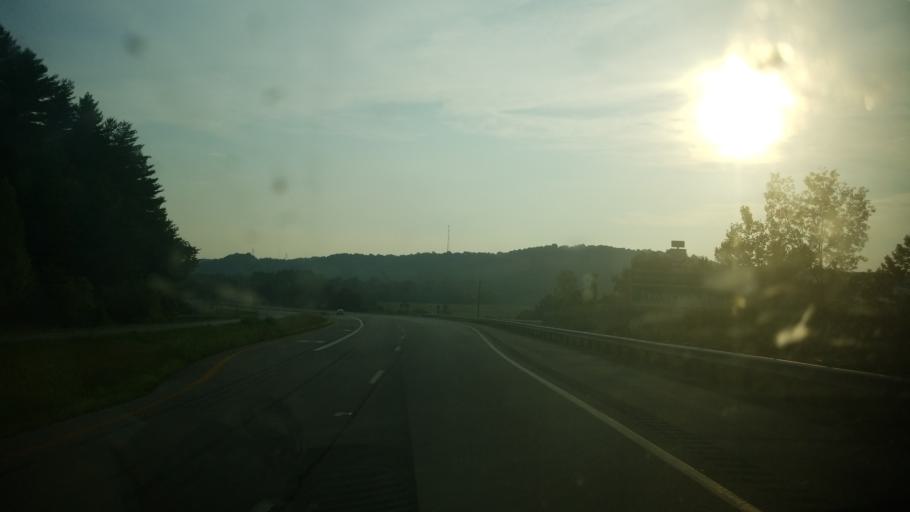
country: US
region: Ohio
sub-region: Pike County
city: Piketon
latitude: 39.0618
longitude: -83.1121
